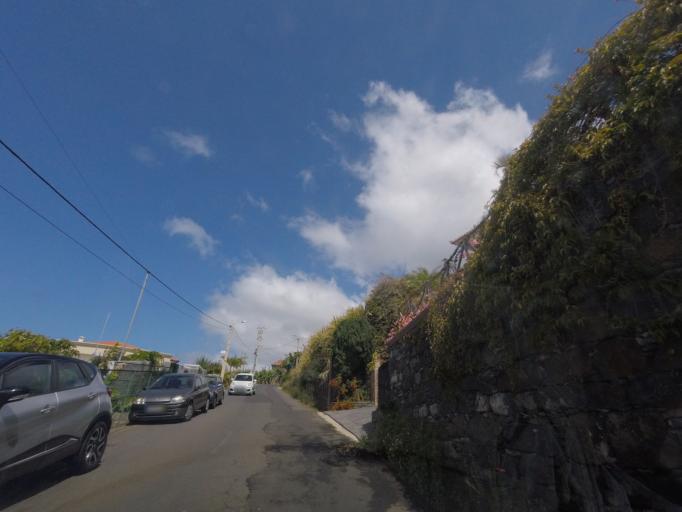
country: PT
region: Madeira
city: Ponta do Sol
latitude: 32.6799
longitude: -17.0816
